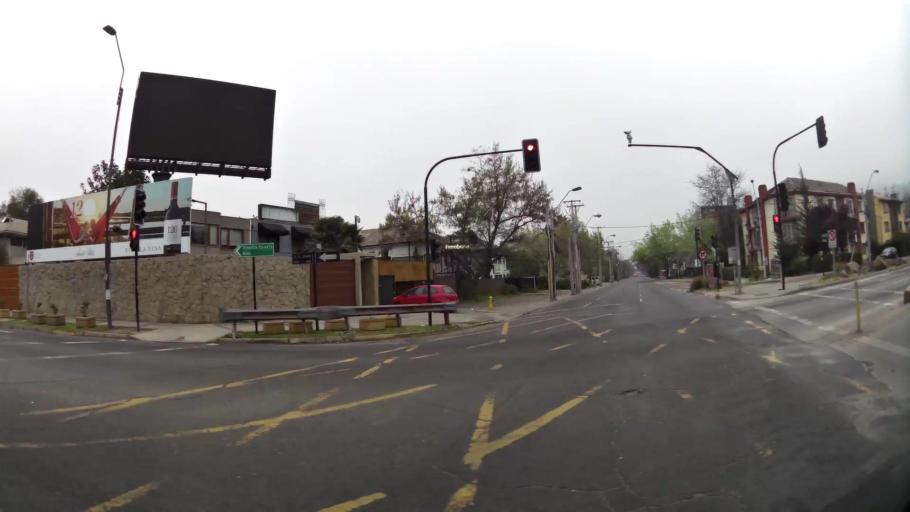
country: CL
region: Santiago Metropolitan
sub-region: Provincia de Santiago
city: Villa Presidente Frei, Nunoa, Santiago, Chile
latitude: -33.4162
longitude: -70.6118
